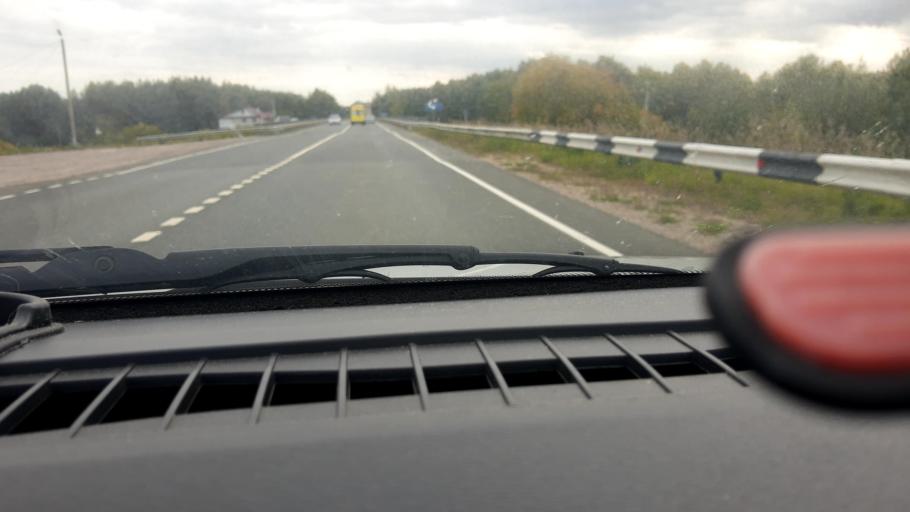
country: RU
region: Nizjnij Novgorod
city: Uren'
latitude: 57.4048
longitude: 45.6848
